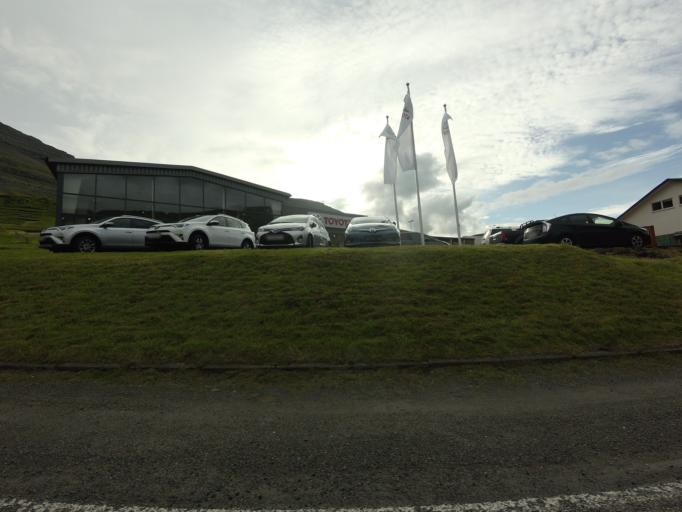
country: FO
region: Nordoyar
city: Klaksvik
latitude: 62.2208
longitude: -6.5745
